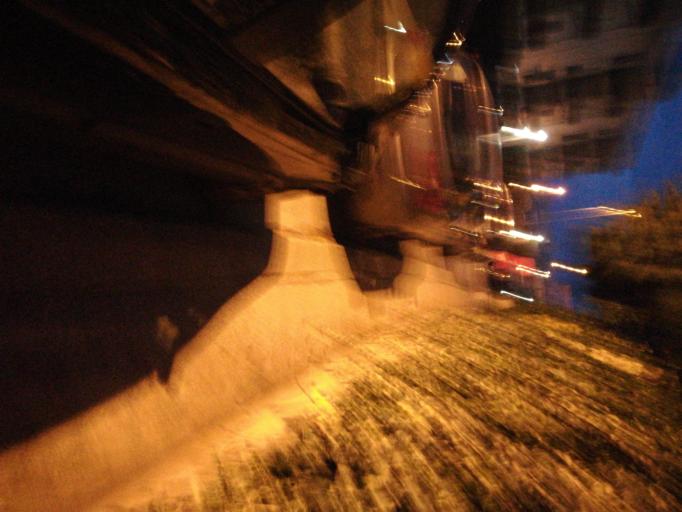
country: IT
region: Apulia
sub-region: Provincia di Bari
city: San Paolo
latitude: 41.1255
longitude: 16.7838
